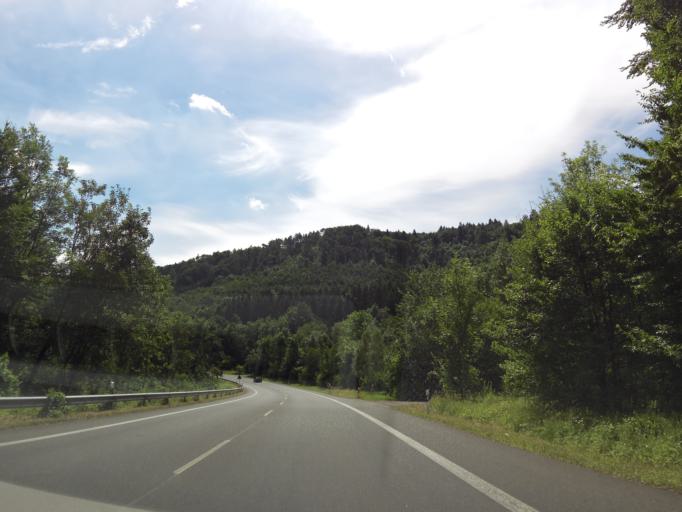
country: DE
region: North Rhine-Westphalia
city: Beverungen
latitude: 51.6365
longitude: 9.3816
